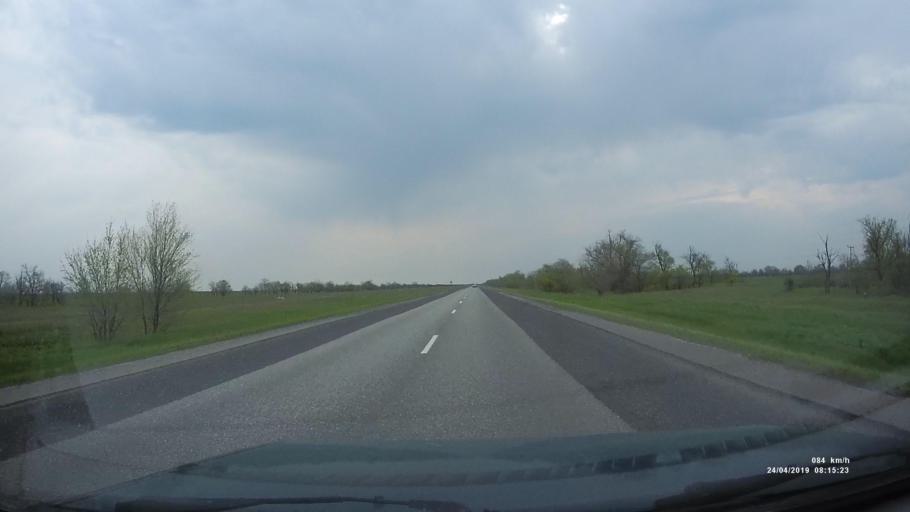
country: RU
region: Kalmykiya
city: Priyutnoye
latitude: 46.1001
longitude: 43.5931
